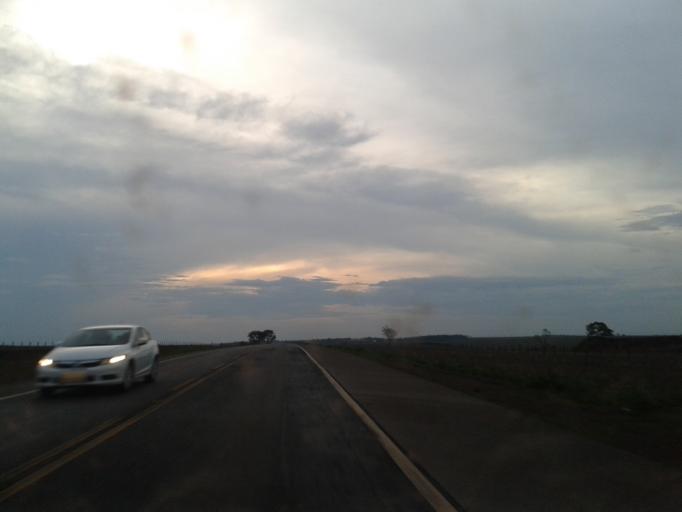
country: BR
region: Goias
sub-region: Santa Helena De Goias
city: Santa Helena de Goias
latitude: -17.8816
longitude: -50.6970
